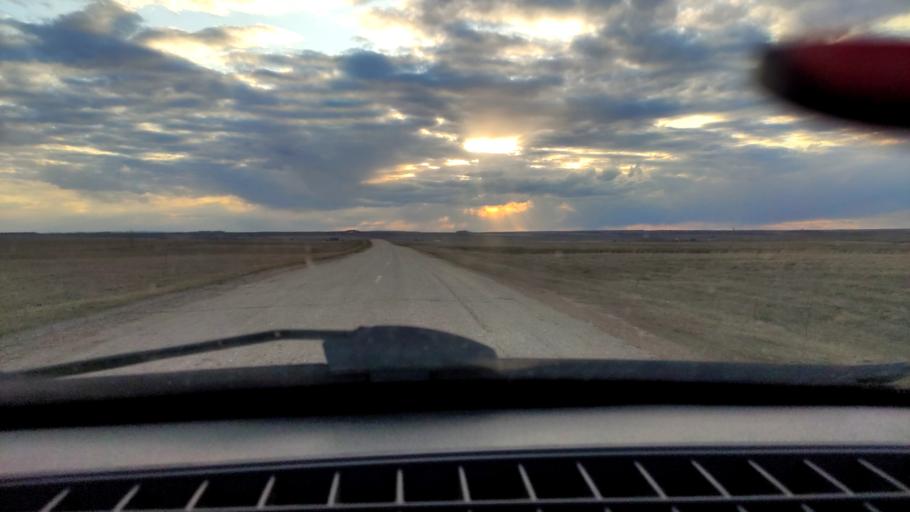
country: RU
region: Bashkortostan
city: Tolbazy
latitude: 54.0140
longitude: 55.5534
